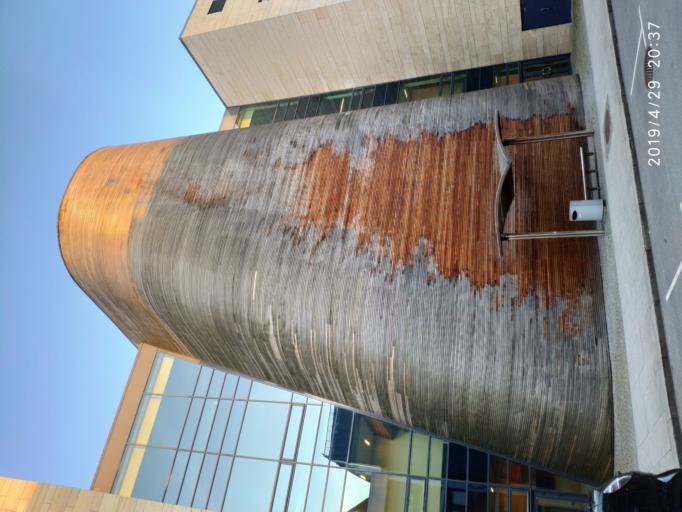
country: NO
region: Rogaland
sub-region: Sandnes
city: Sandnes
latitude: 58.8507
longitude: 5.7403
